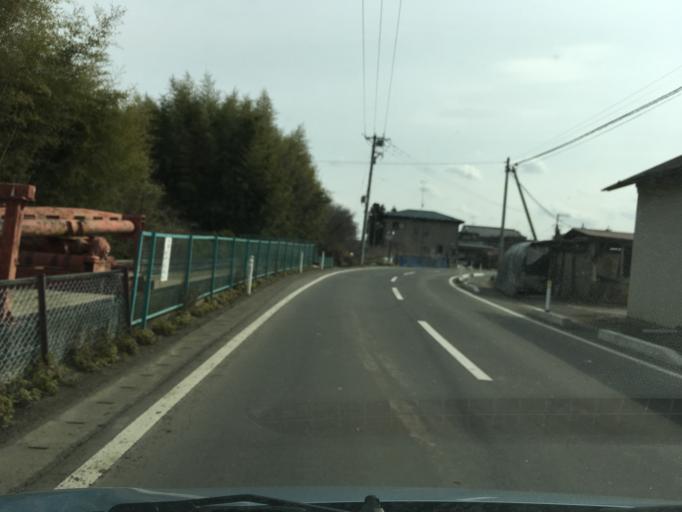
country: JP
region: Miyagi
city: Wakuya
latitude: 38.7197
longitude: 141.2427
